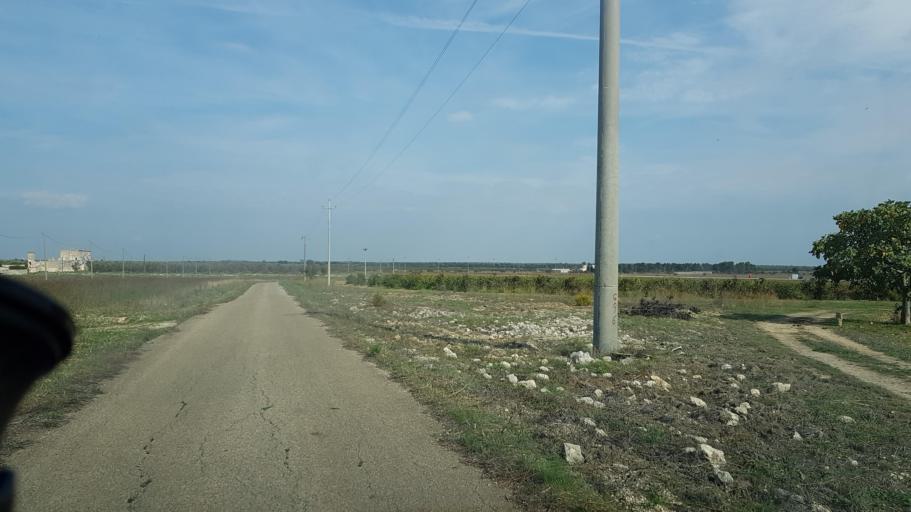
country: IT
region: Apulia
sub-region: Provincia di Brindisi
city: San Pancrazio Salentino
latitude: 40.4360
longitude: 17.8518
